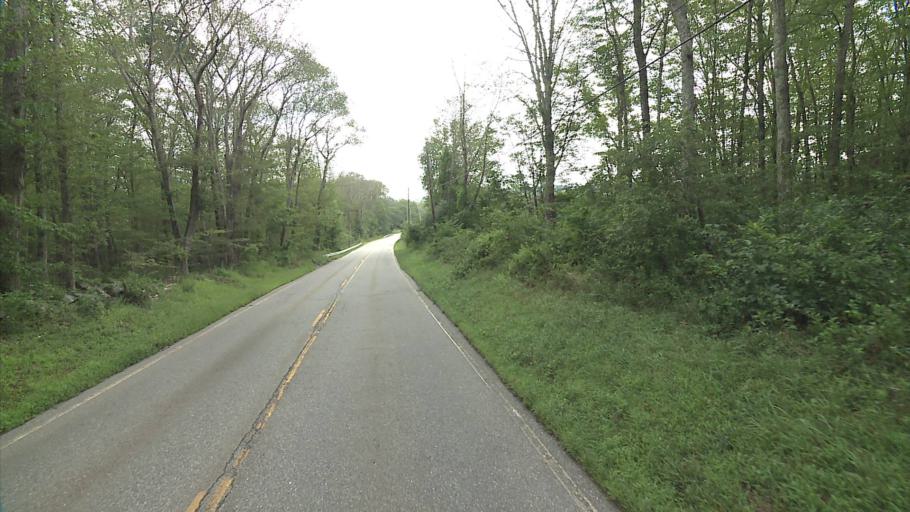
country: US
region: Connecticut
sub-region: New London County
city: Colchester
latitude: 41.4608
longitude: -72.2967
